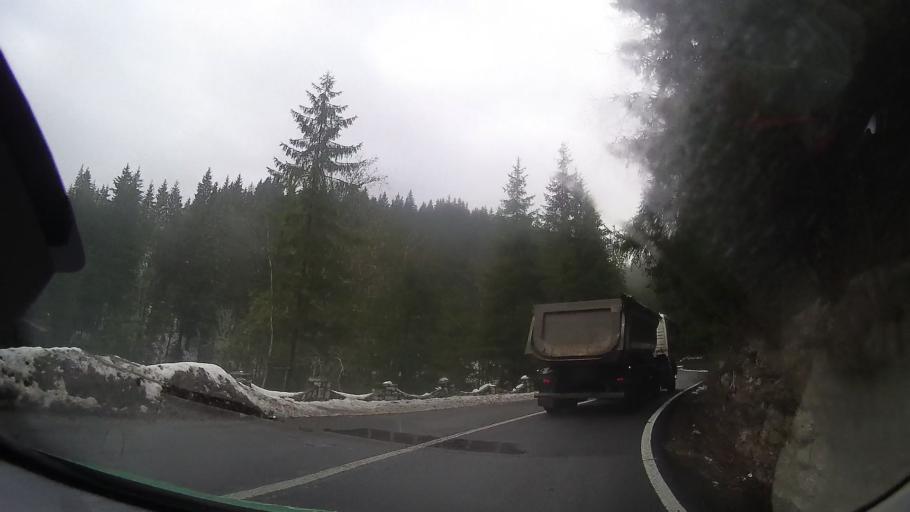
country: RO
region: Harghita
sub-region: Oras Balan
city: Balan
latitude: 46.7755
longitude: 25.7415
